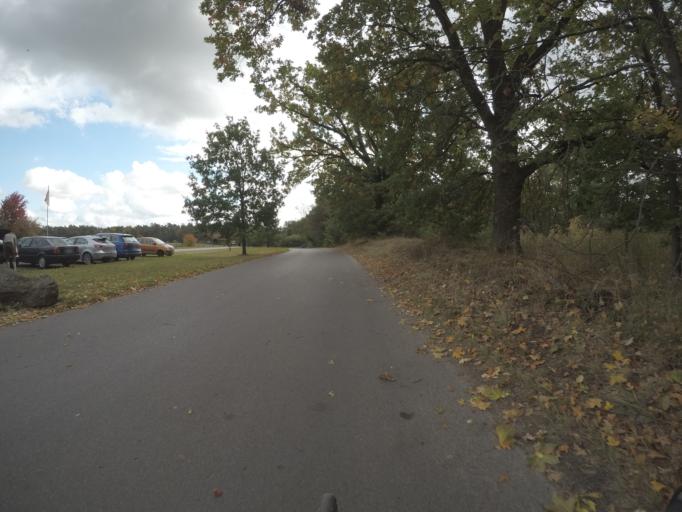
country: DE
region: Brandenburg
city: Strausberg
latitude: 52.6112
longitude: 13.9132
